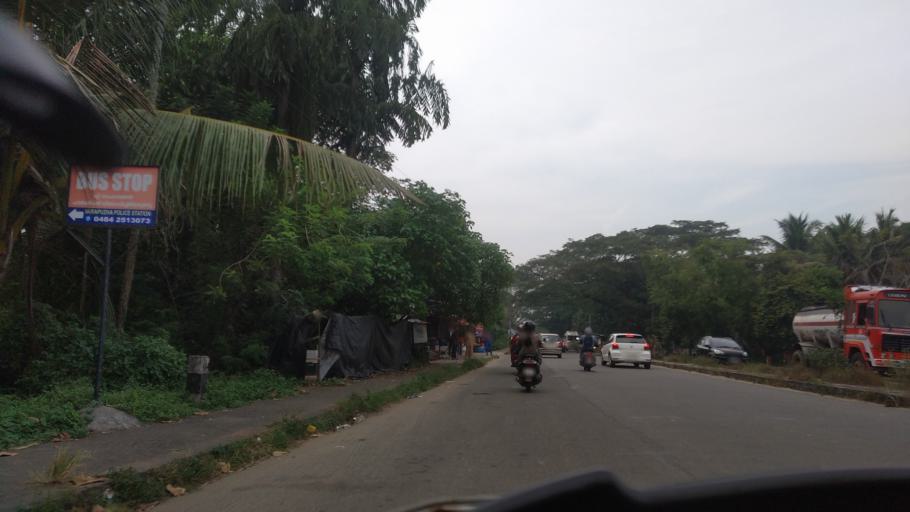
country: IN
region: Kerala
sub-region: Ernakulam
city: Elur
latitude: 10.0780
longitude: 76.2755
